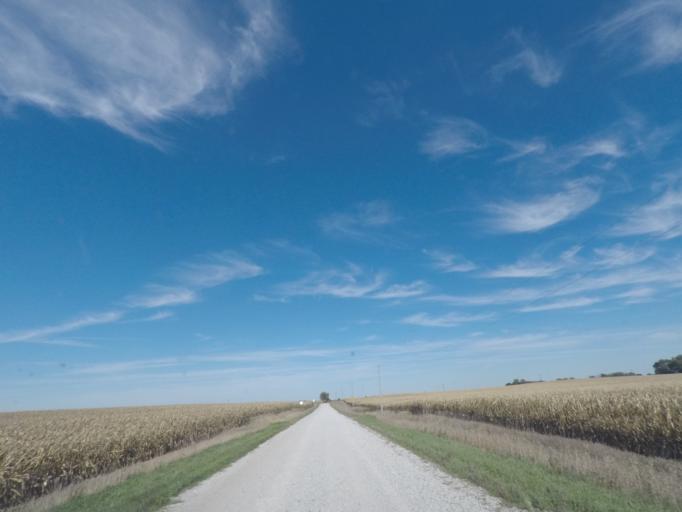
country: US
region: Iowa
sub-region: Story County
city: Nevada
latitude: 42.0200
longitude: -93.3573
